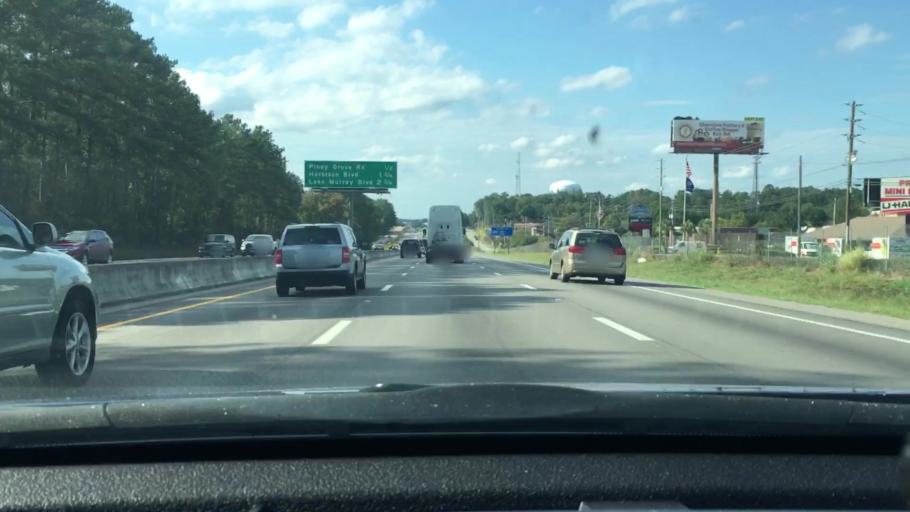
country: US
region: South Carolina
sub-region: Lexington County
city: Saint Andrews
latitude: 34.0583
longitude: -81.1324
